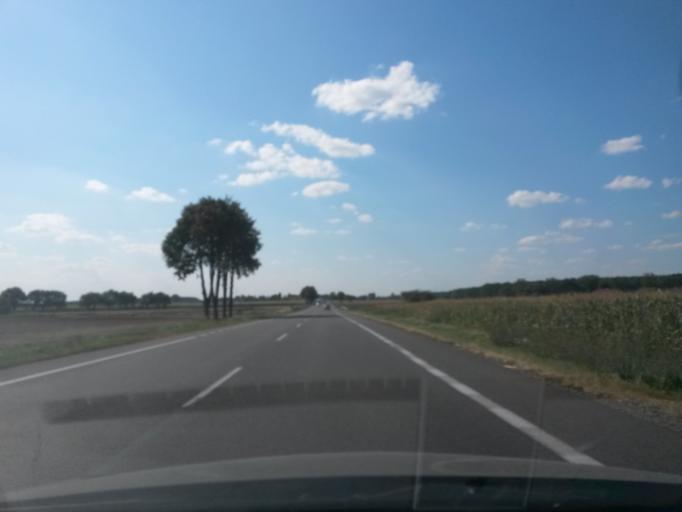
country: PL
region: Masovian Voivodeship
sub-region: Powiat plocki
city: Bulkowo
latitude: 52.6421
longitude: 20.1234
